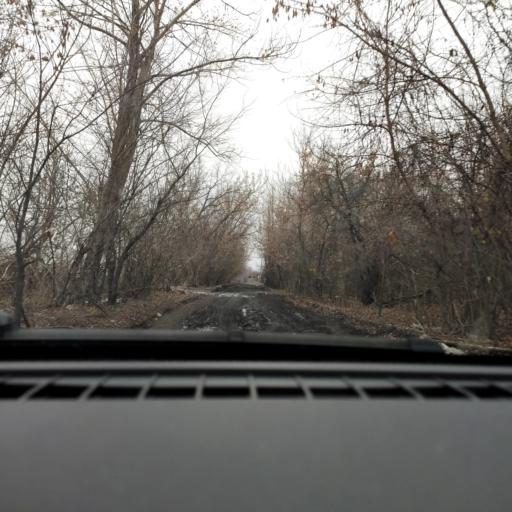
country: RU
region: Voronezj
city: Maslovka
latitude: 51.6087
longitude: 39.2722
